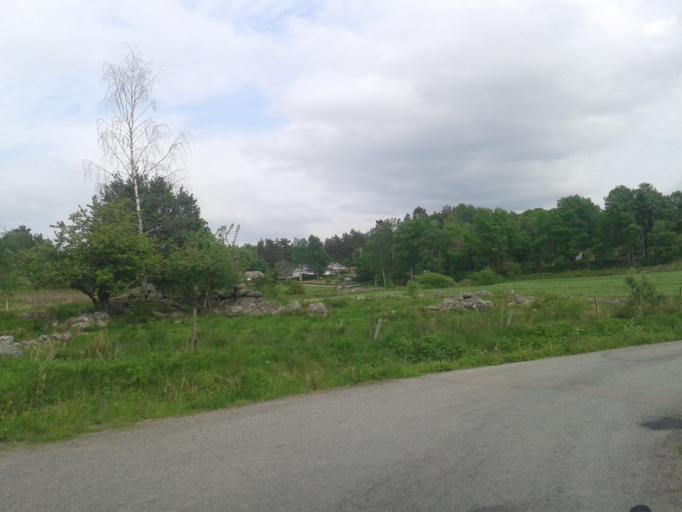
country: SE
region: Vaestra Goetaland
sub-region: Kungalvs Kommun
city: Kungalv
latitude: 57.9040
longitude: 11.9518
